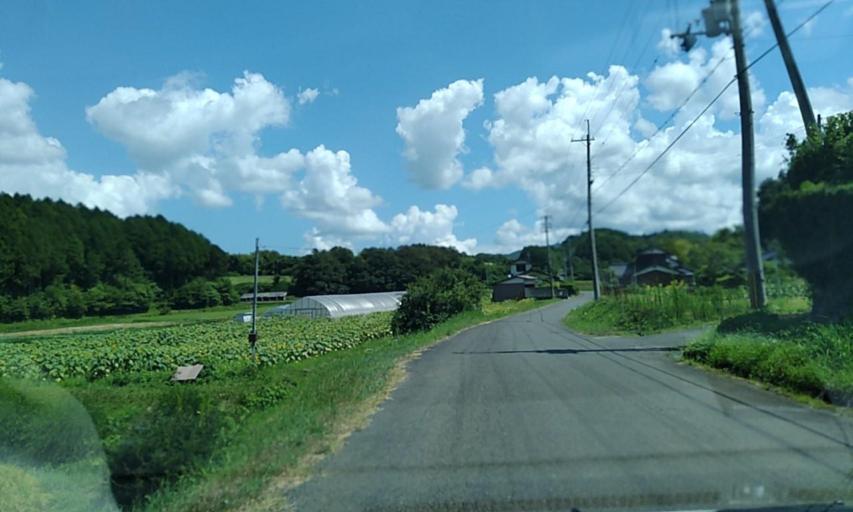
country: JP
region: Kyoto
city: Ayabe
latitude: 35.3469
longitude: 135.2285
